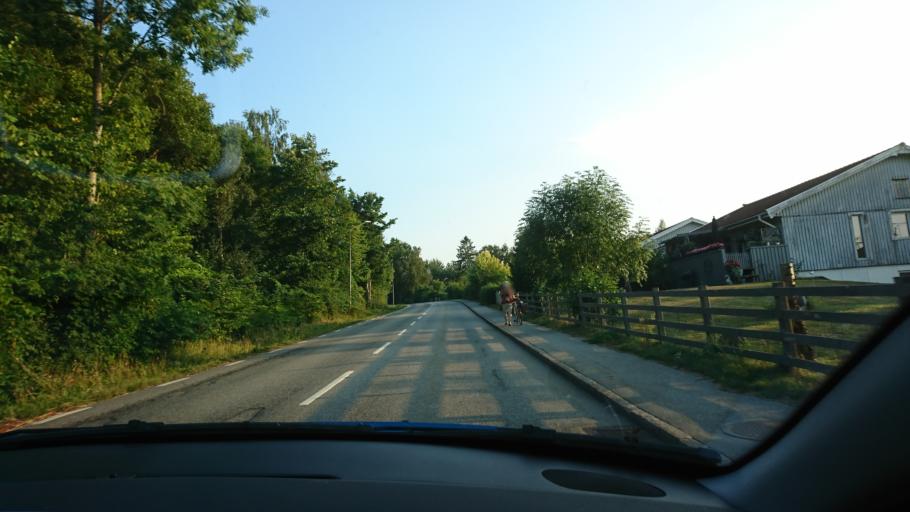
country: SE
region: Skane
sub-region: Simrishamns Kommun
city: Kivik
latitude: 55.6882
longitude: 14.1553
